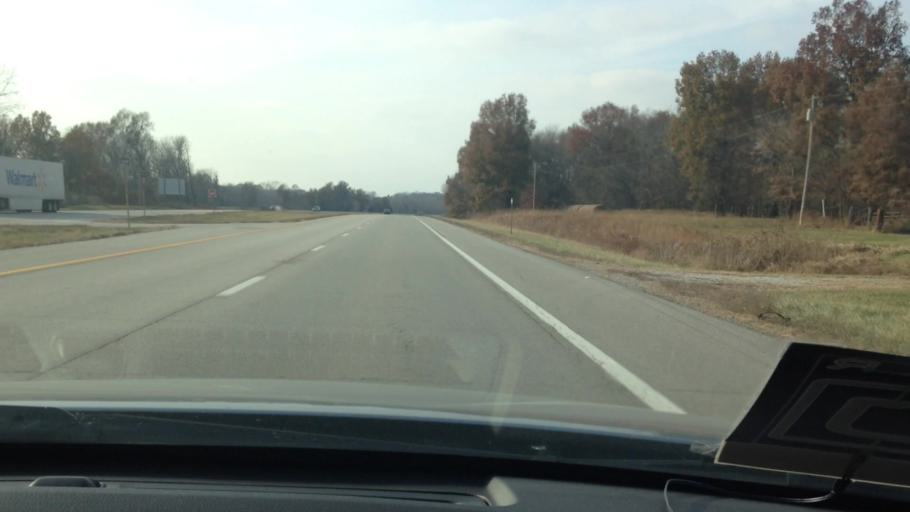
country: US
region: Missouri
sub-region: Cass County
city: Garden City
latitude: 38.5056
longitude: -94.0891
